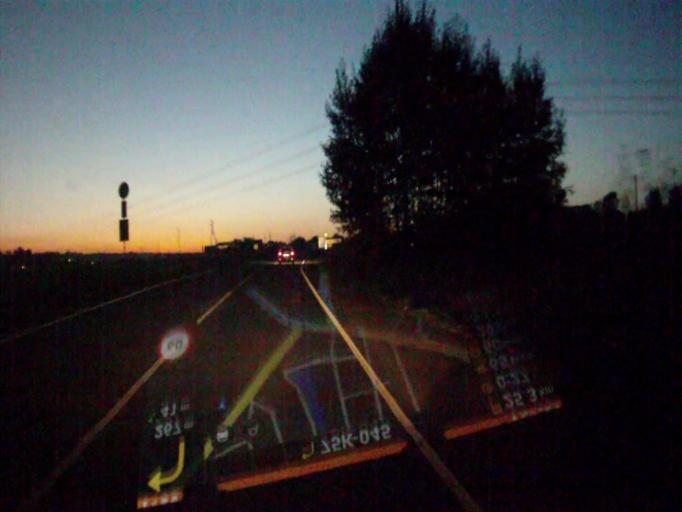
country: RU
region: Chelyabinsk
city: Chebarkul'
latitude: 55.2274
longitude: 60.4551
